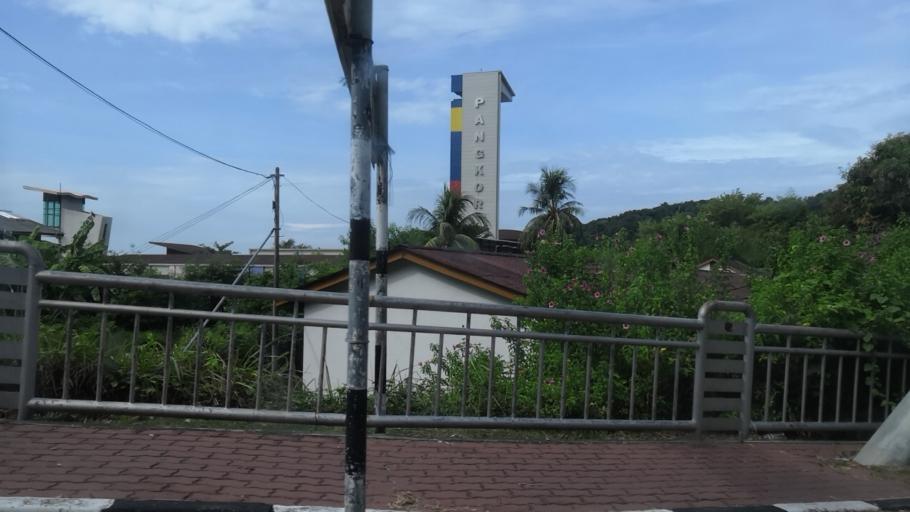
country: MY
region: Perak
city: Lumut
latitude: 4.2145
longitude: 100.5760
